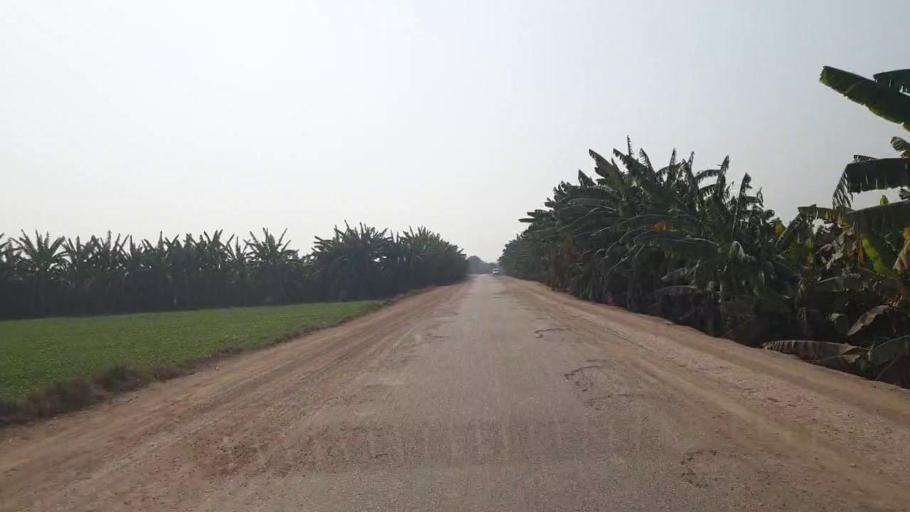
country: PK
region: Sindh
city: Hala
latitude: 25.8974
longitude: 68.4424
